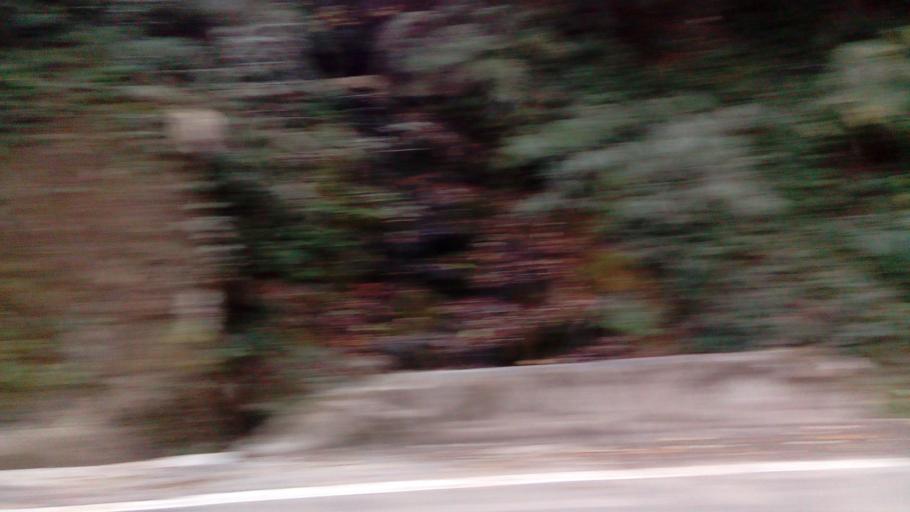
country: TW
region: Taiwan
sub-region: Hualien
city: Hualian
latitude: 24.3477
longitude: 121.3196
